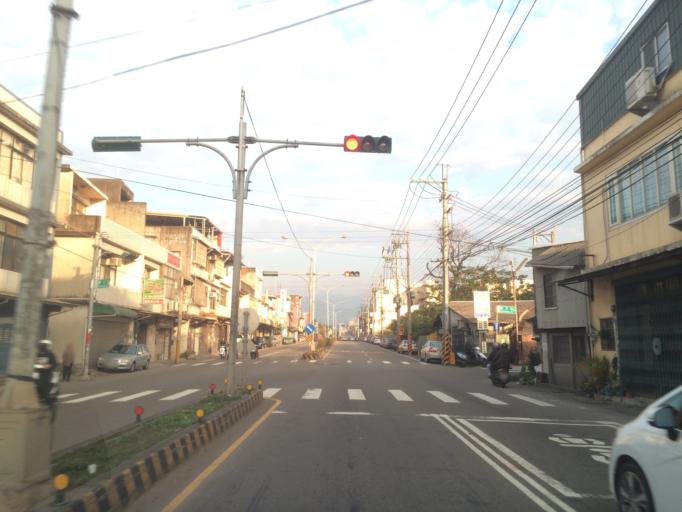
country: TW
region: Taiwan
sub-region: Hsinchu
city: Zhubei
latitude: 24.7219
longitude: 121.1084
